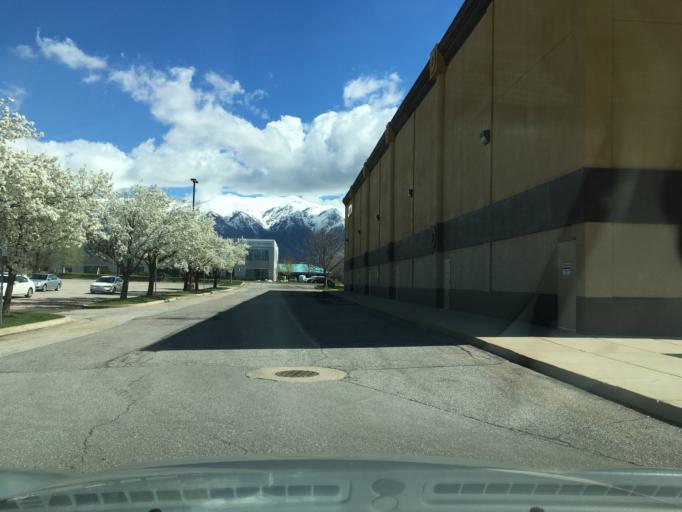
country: US
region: Utah
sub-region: Davis County
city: Layton
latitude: 41.0822
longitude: -111.9795
